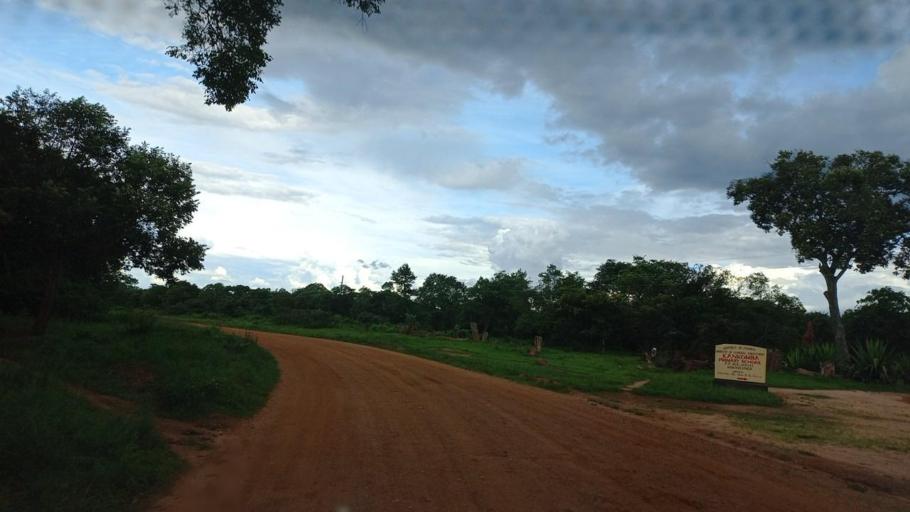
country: ZM
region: North-Western
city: Mwinilunga
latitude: -11.7743
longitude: 24.4041
